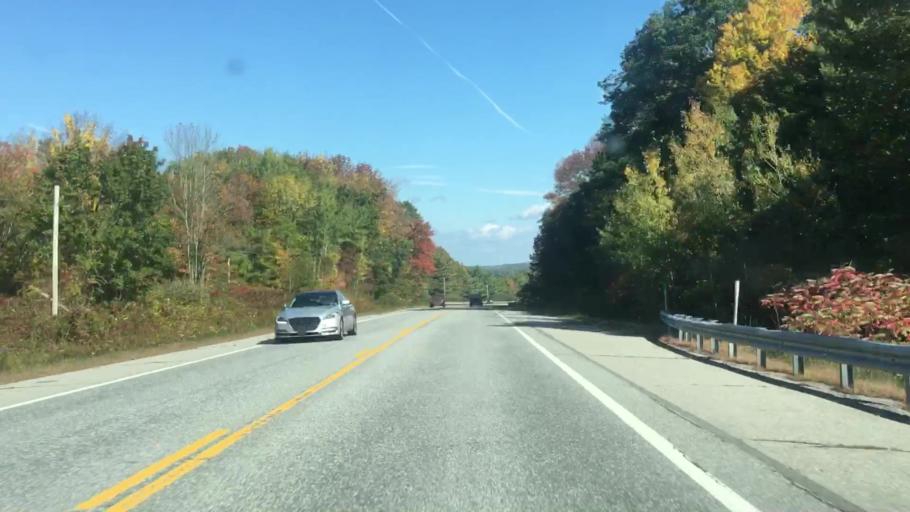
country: US
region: Maine
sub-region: Lincoln County
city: Damariscotta
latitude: 44.0374
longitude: -69.5377
